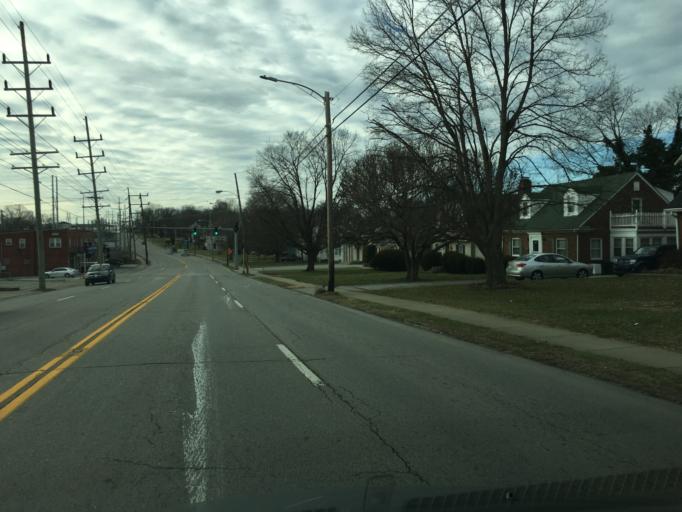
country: US
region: Kentucky
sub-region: Franklin County
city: Frankfort
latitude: 38.2052
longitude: -84.8398
